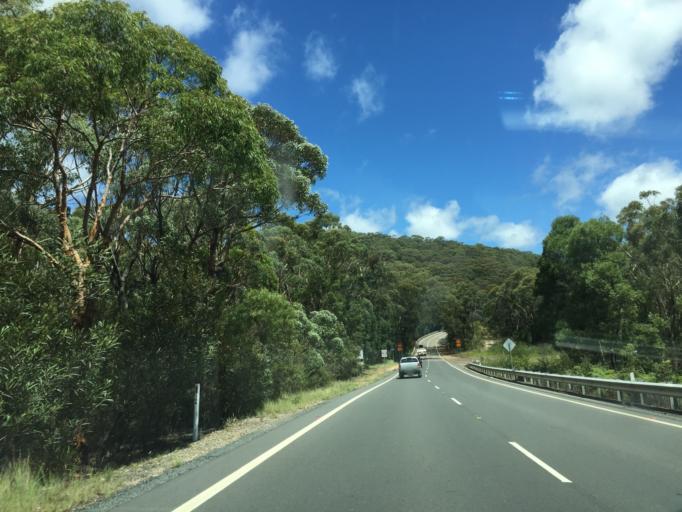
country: AU
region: New South Wales
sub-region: Blue Mountains Municipality
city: Blackheath
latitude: -33.5381
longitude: 150.4340
